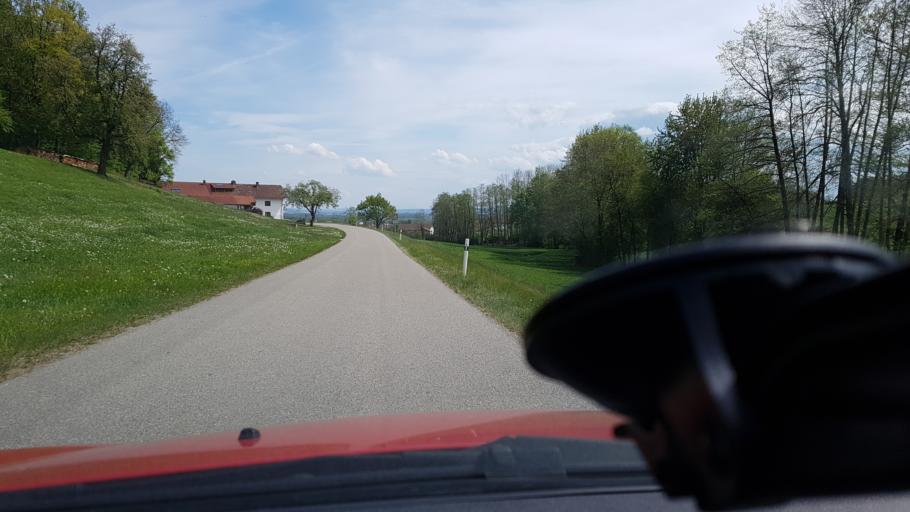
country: DE
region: Bavaria
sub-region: Lower Bavaria
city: Ering
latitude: 48.3119
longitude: 13.1200
